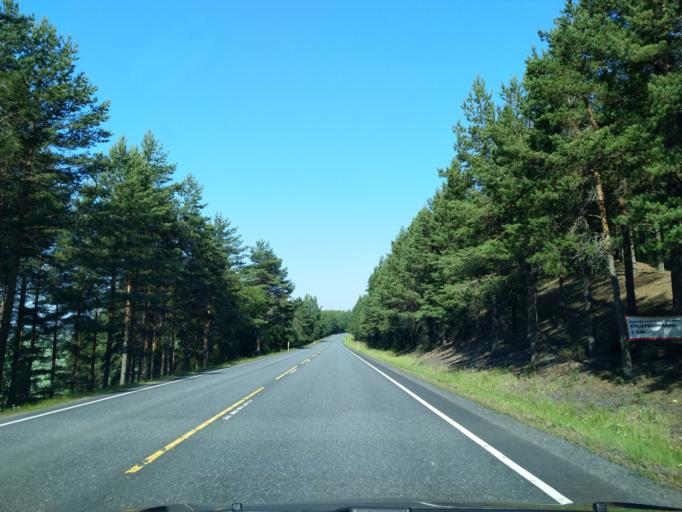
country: FI
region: Haeme
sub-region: Forssa
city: Humppila
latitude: 60.9657
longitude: 23.3002
